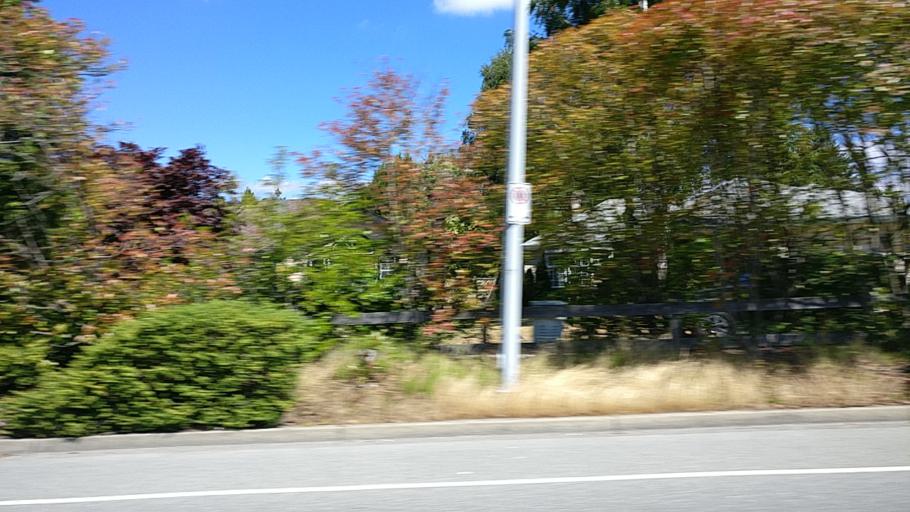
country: CA
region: British Columbia
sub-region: Greater Vancouver Regional District
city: White Rock
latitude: 49.0384
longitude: -122.8093
